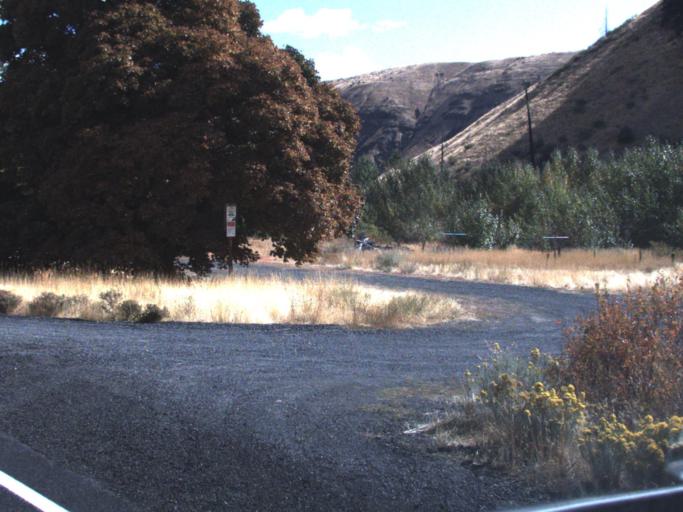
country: US
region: Washington
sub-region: Yakima County
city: Tieton
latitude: 46.7196
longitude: -120.8319
